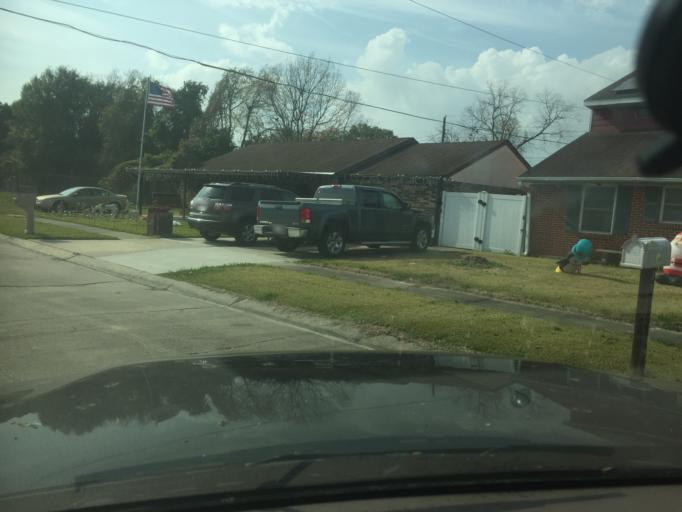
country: US
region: Louisiana
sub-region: Jefferson Parish
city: Avondale
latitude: 29.9136
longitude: -90.2007
